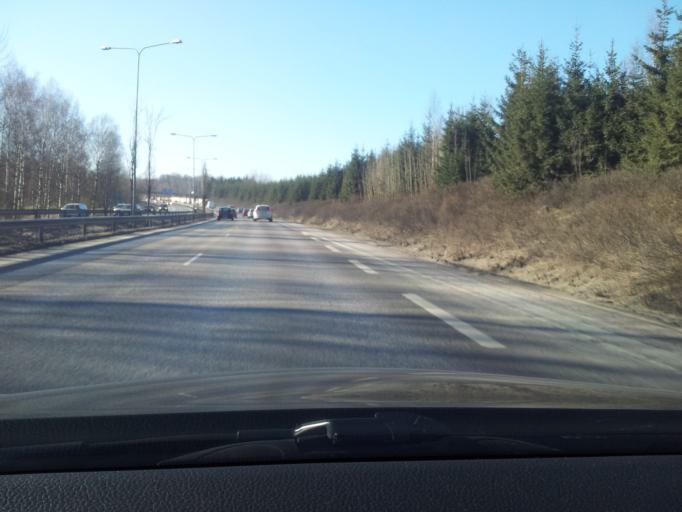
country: FI
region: Uusimaa
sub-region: Helsinki
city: Helsinki
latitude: 60.2438
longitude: 24.9710
